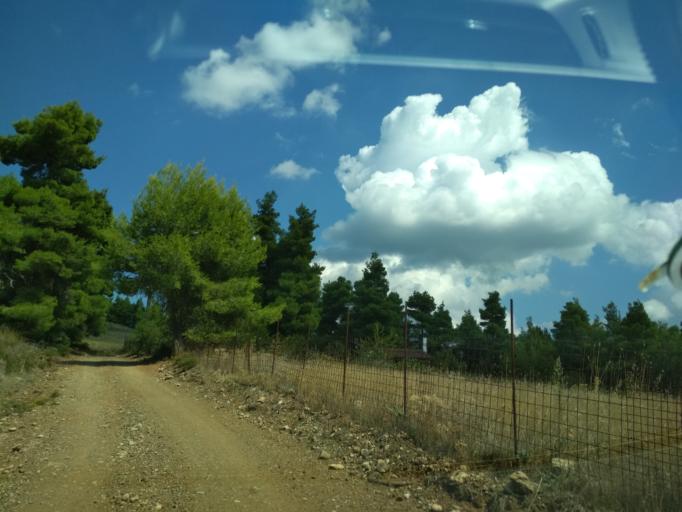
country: GR
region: Central Greece
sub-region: Nomos Evvoias
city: Roviai
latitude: 38.8370
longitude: 23.2788
